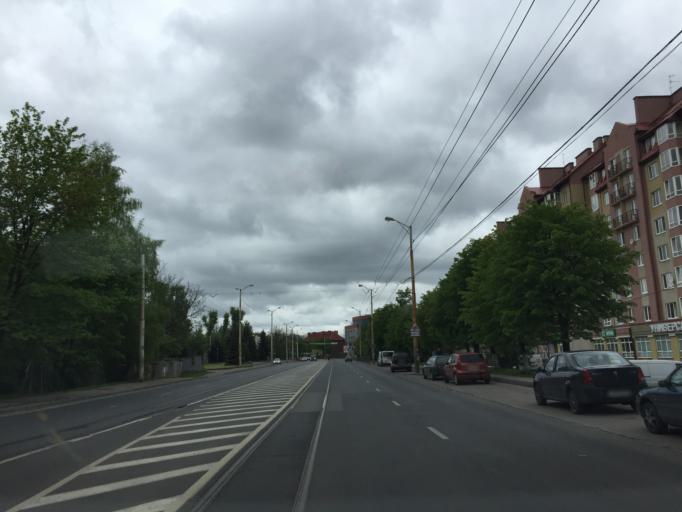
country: RU
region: Kaliningrad
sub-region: Gorod Kaliningrad
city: Kaliningrad
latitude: 54.6934
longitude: 20.4742
